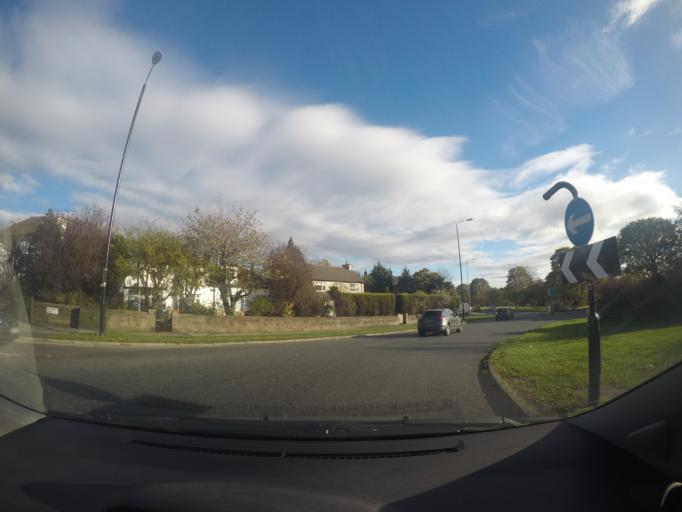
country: GB
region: England
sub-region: City and Borough of Leeds
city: Shadwell
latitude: 53.8372
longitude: -1.4723
